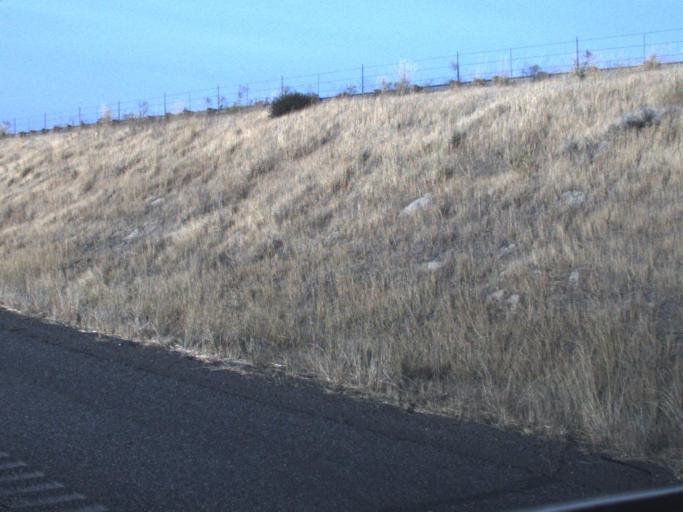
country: US
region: Washington
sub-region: Benton County
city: Highland
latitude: 46.0419
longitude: -119.2242
